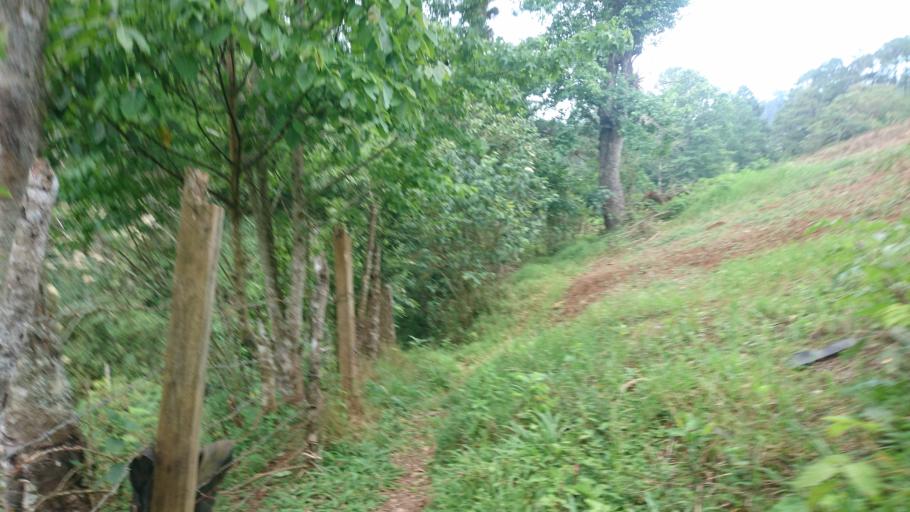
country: GT
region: Huehuetenango
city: Union
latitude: 16.1323
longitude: -91.7273
